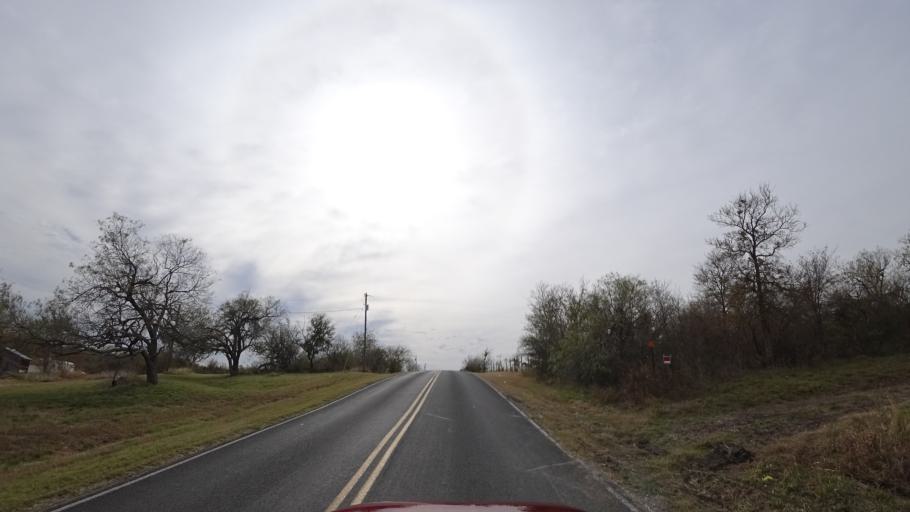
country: US
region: Texas
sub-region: Travis County
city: Garfield
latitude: 30.1464
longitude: -97.5790
